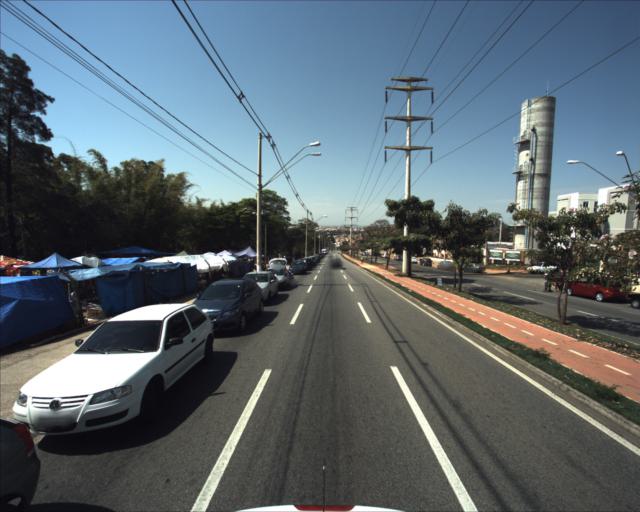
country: BR
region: Sao Paulo
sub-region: Sorocaba
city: Sorocaba
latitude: -23.4466
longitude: -47.5010
